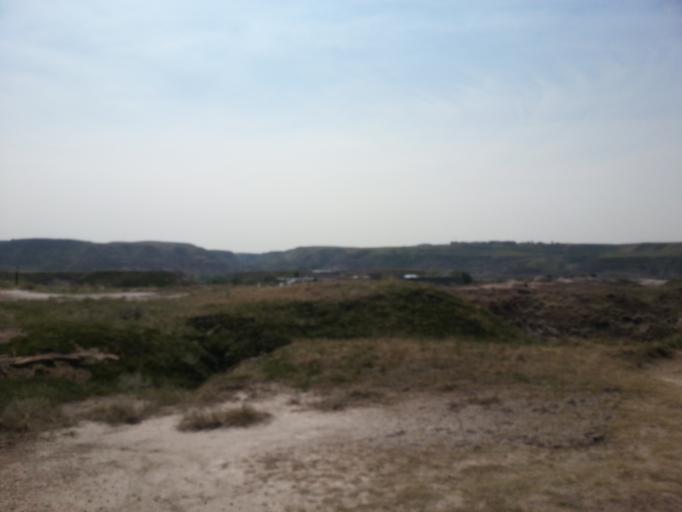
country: CA
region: Alberta
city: Three Hills
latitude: 51.4823
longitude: -112.7882
